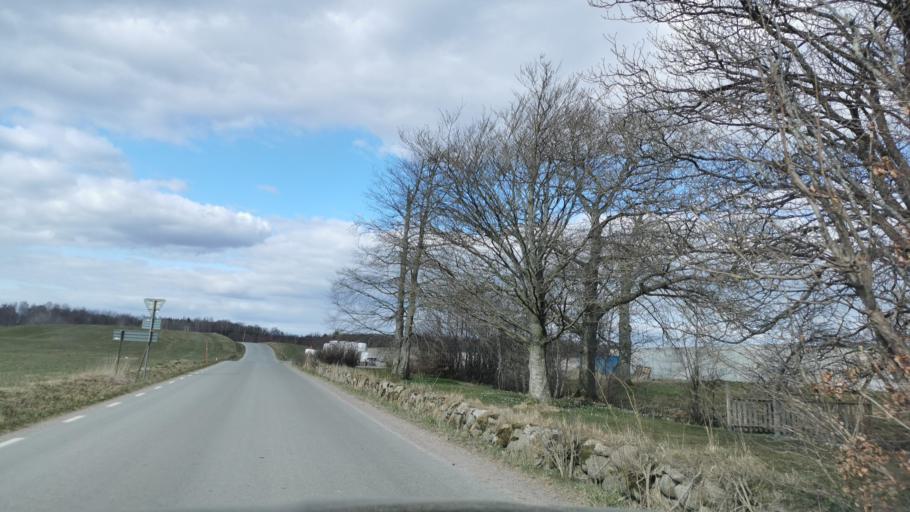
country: SE
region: Skane
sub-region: Sjobo Kommun
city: Sjoebo
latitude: 55.7385
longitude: 13.8367
